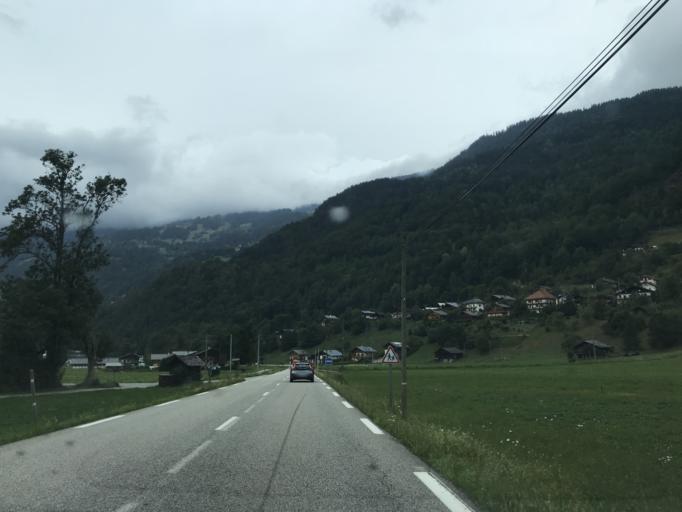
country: FR
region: Rhone-Alpes
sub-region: Departement de la Savoie
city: Beaufort
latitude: 45.7236
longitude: 6.5547
